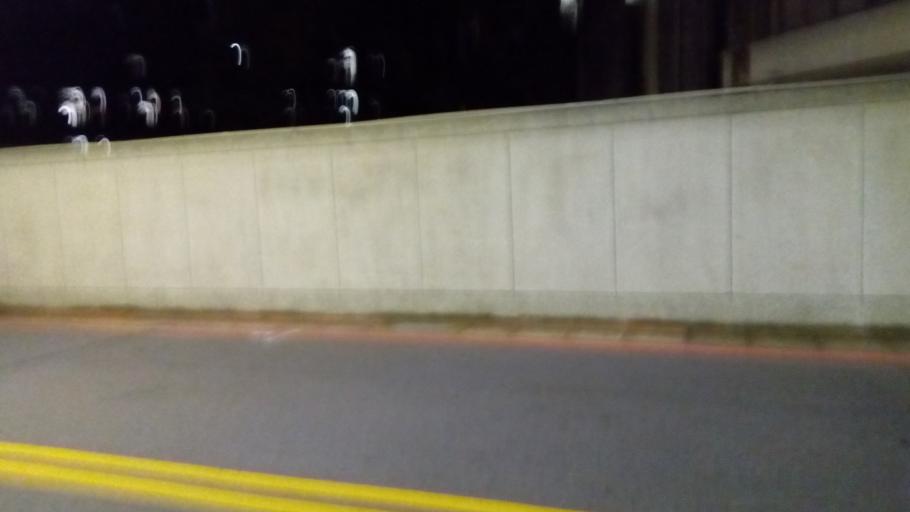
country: TW
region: Taipei
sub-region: Taipei
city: Banqiao
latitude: 25.0343
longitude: 121.4310
